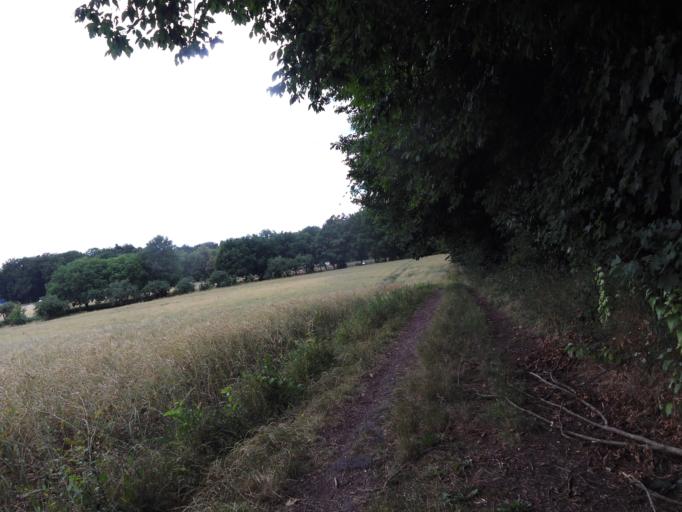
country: DE
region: Bavaria
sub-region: Regierungsbezirk Unterfranken
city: Reichenberg
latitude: 49.7569
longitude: 9.9154
